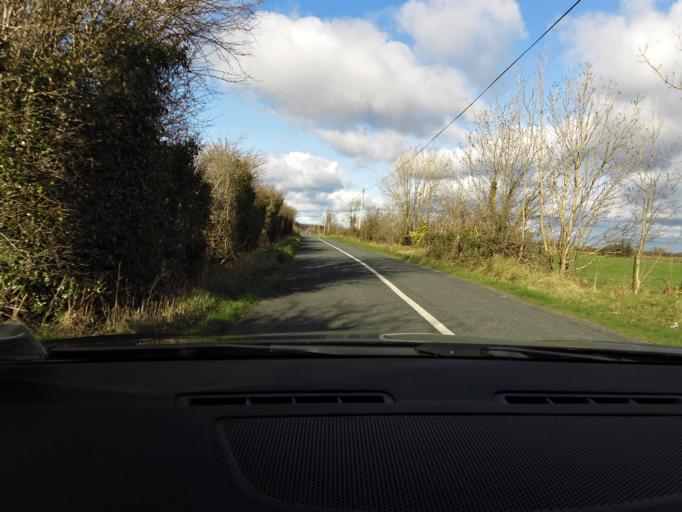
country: IE
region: Connaught
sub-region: County Galway
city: Athenry
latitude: 53.4456
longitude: -8.5590
